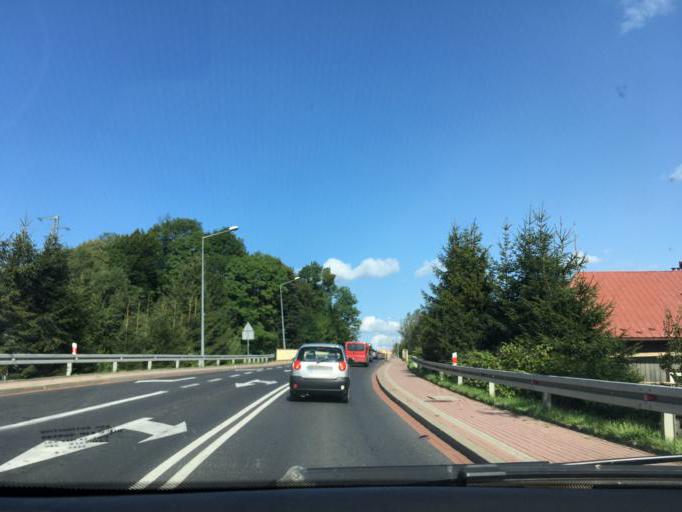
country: PL
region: Subcarpathian Voivodeship
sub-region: Powiat sanocki
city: Zagorz
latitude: 49.5146
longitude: 22.2667
